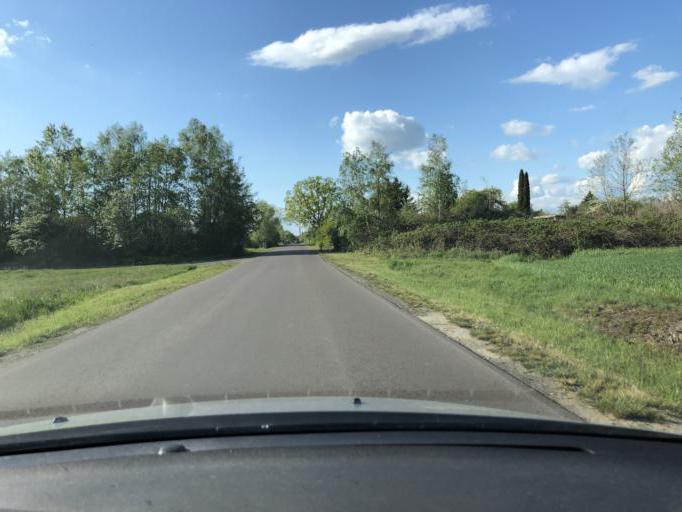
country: DE
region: Saxony
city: Deutzen
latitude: 51.1256
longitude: 12.4560
